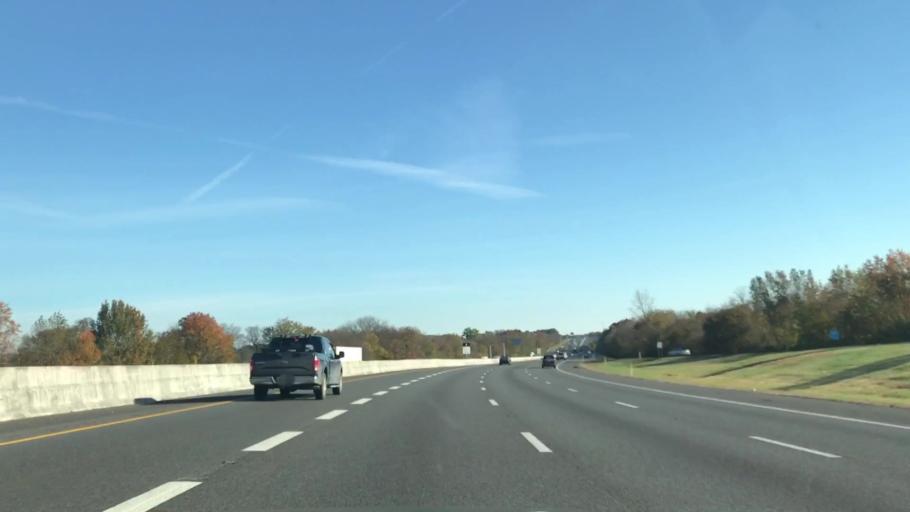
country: US
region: Tennessee
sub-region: Williamson County
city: Brentwood Estates
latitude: 35.9990
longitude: -86.7960
